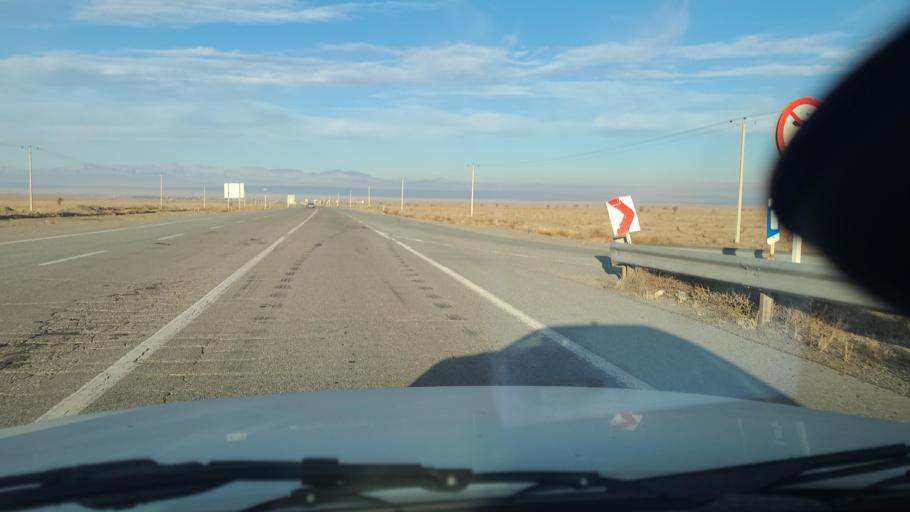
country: IR
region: Razavi Khorasan
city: Neqab
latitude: 36.5146
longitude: 57.5418
